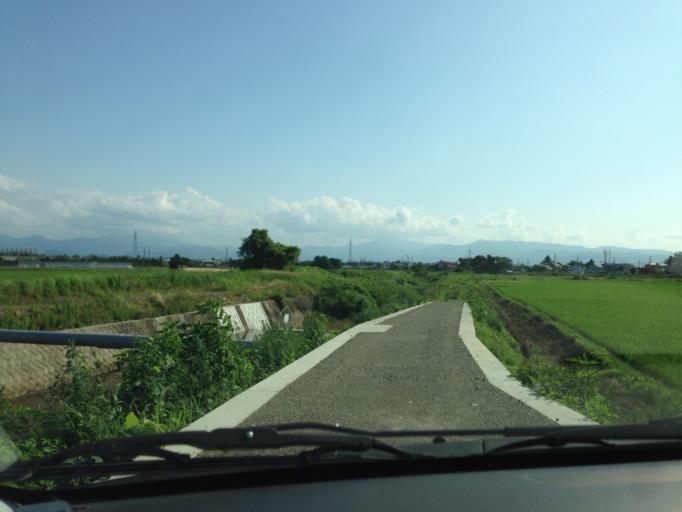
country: JP
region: Fukushima
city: Kitakata
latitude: 37.5323
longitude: 139.9355
